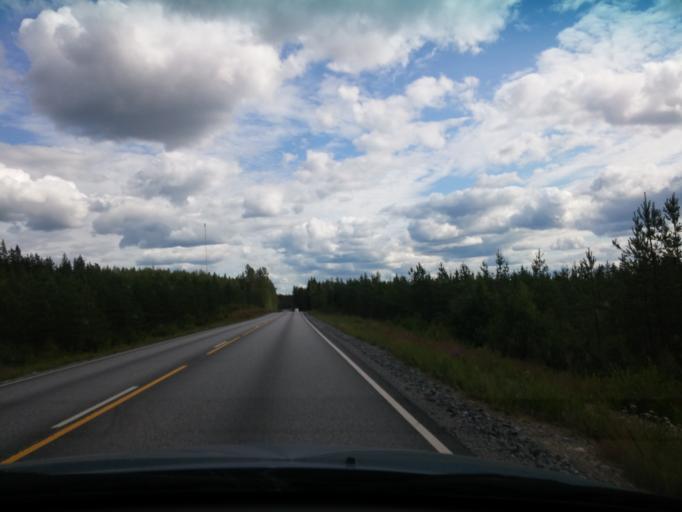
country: FI
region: Central Finland
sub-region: Keuruu
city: Multia
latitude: 62.5105
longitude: 24.6726
